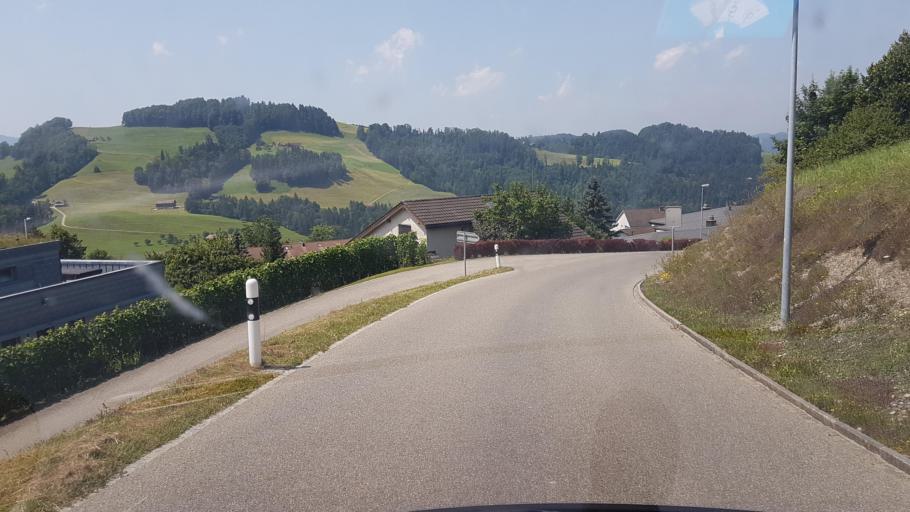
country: CH
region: Saint Gallen
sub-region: Wahlkreis Toggenburg
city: Mogelsberg
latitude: 47.3601
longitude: 9.1362
